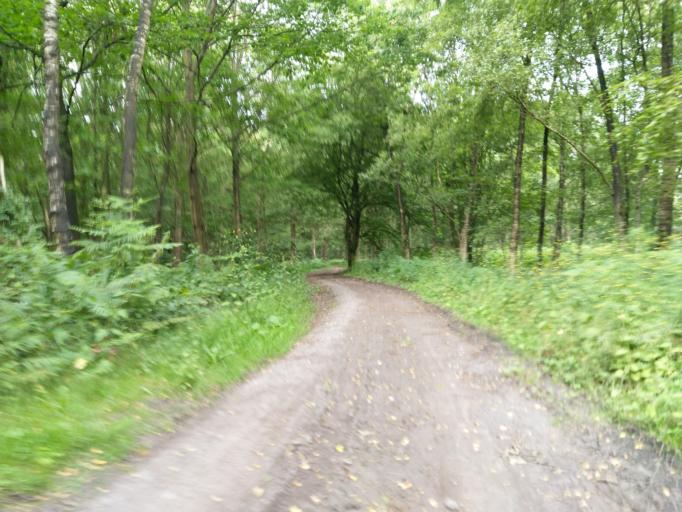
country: BE
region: Wallonia
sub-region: Province du Hainaut
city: Saint-Ghislain
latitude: 50.5013
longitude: 3.8294
